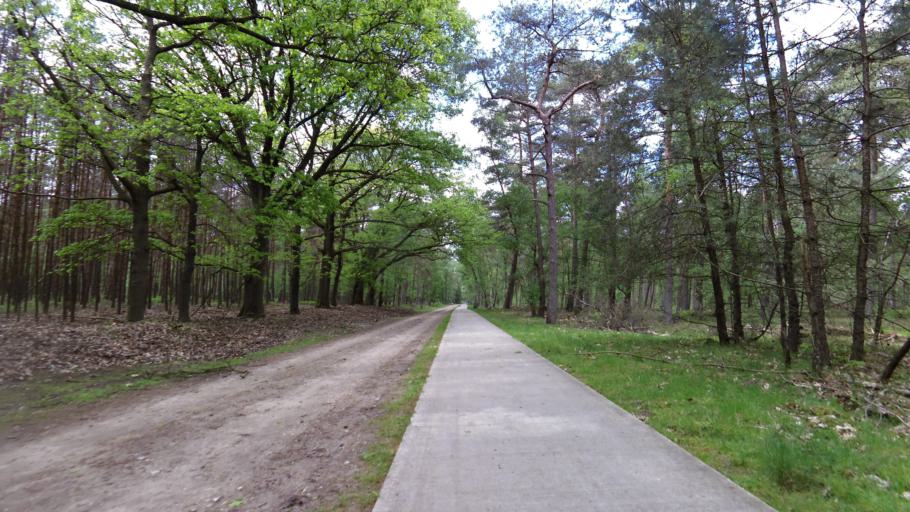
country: NL
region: Gelderland
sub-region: Gemeente Brummen
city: Eerbeek
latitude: 52.0743
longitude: 6.0580
